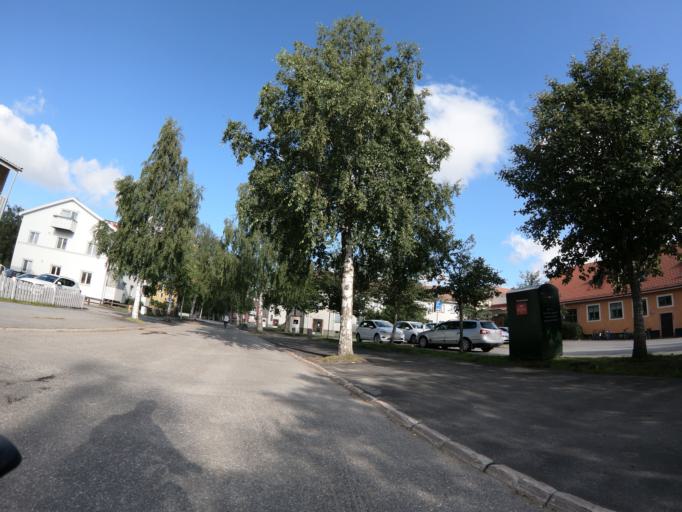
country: SE
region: Vaesterbotten
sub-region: Umea Kommun
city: Umea
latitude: 63.8295
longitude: 20.2758
